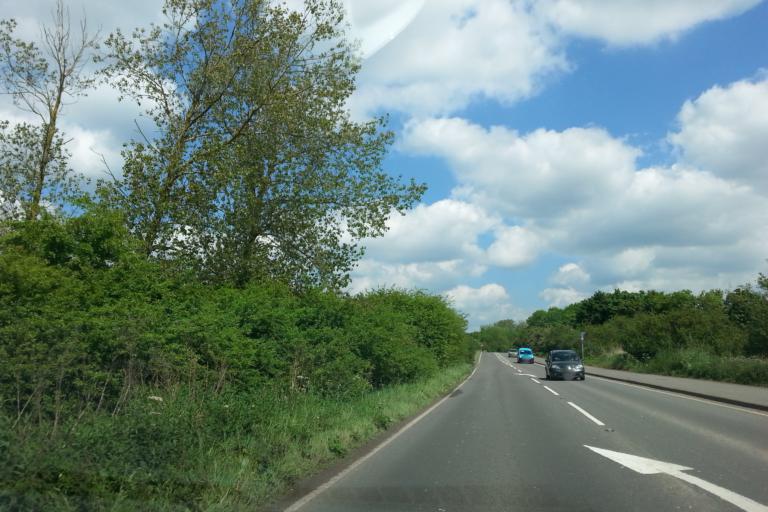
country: GB
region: England
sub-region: Cambridgeshire
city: Yaxley
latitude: 52.5238
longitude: -0.2687
